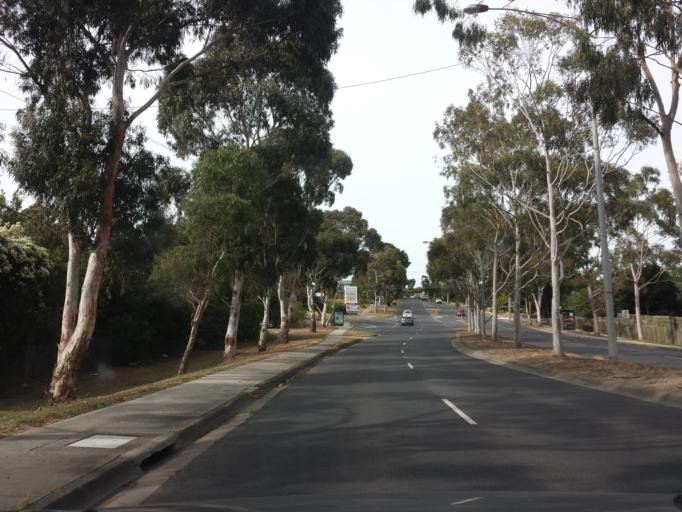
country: AU
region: Victoria
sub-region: Monash
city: Notting Hill
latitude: -37.8935
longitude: 145.1257
